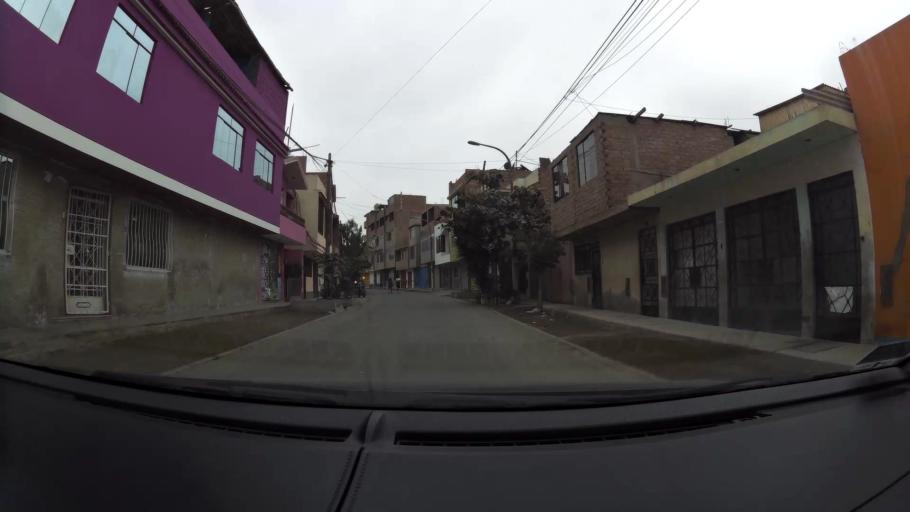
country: PE
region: Lima
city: Ventanilla
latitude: -11.9349
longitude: -77.0864
